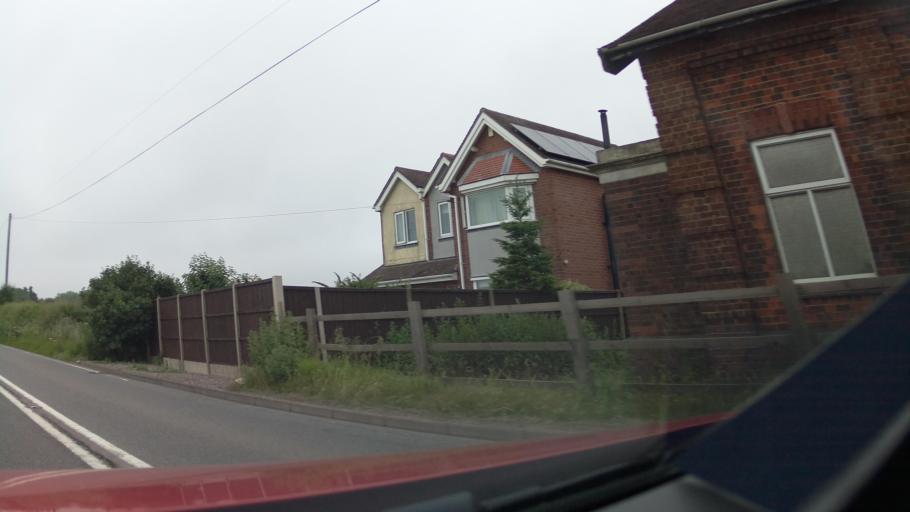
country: GB
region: England
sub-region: Leicestershire
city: Donisthorpe
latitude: 52.7122
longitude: -1.5555
